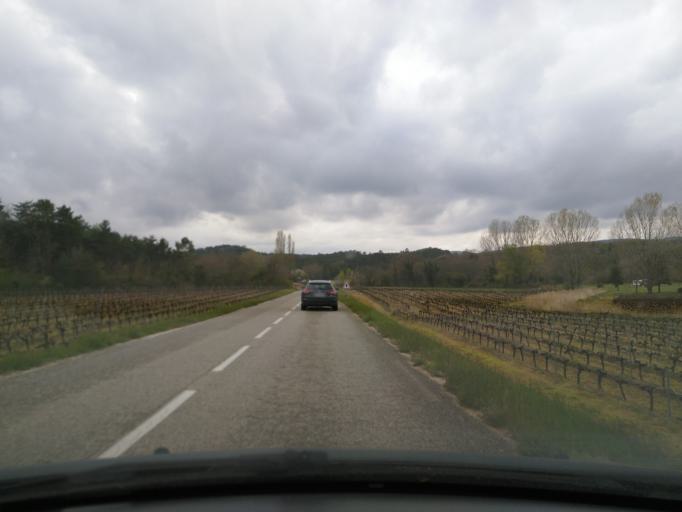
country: FR
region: Languedoc-Roussillon
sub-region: Departement du Gard
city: Barjac
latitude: 44.3556
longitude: 4.3847
